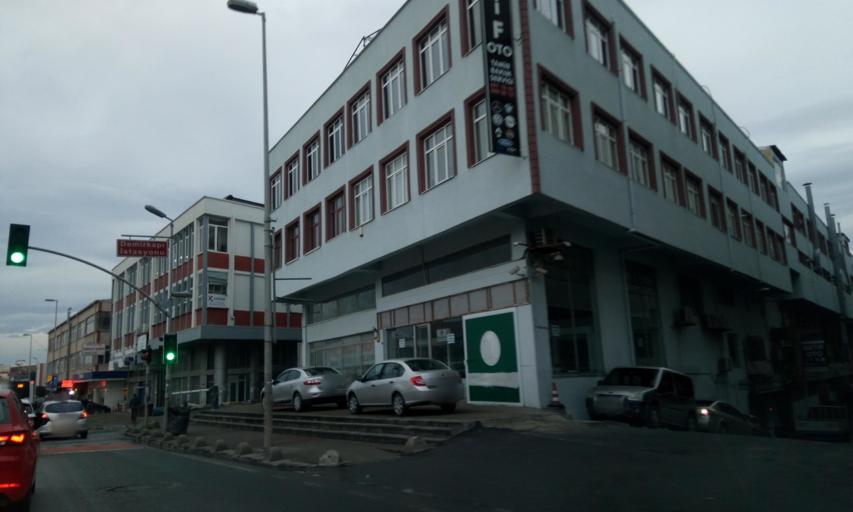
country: TR
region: Istanbul
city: Istanbul
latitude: 41.0376
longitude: 28.9229
